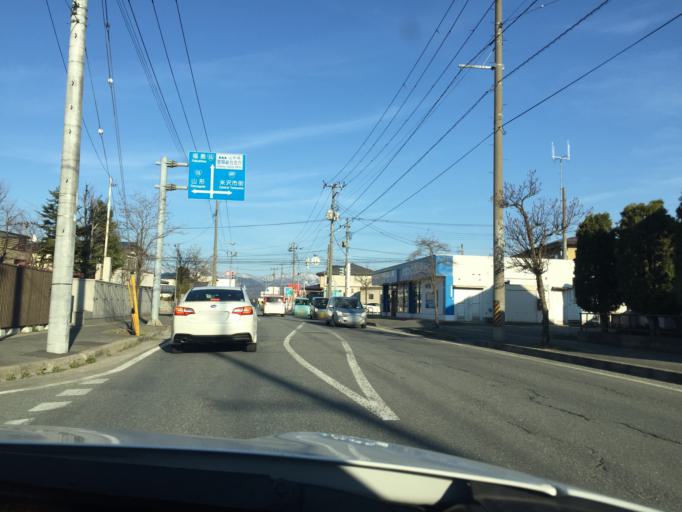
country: JP
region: Yamagata
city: Yonezawa
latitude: 37.9265
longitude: 140.1121
